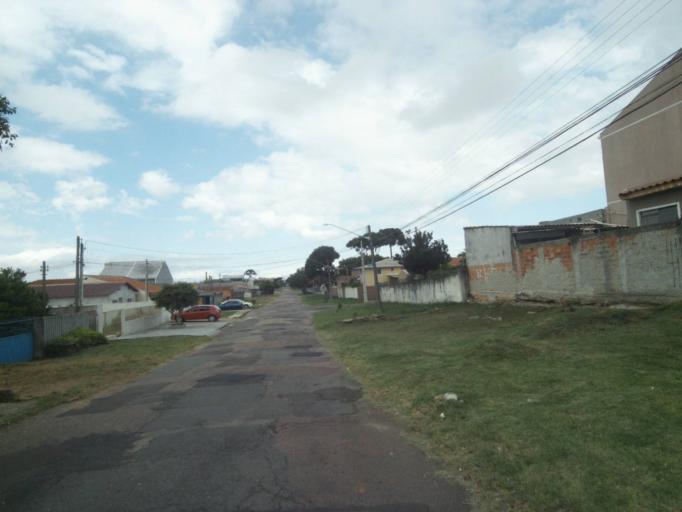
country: BR
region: Parana
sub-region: Pinhais
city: Pinhais
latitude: -25.4498
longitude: -49.2107
